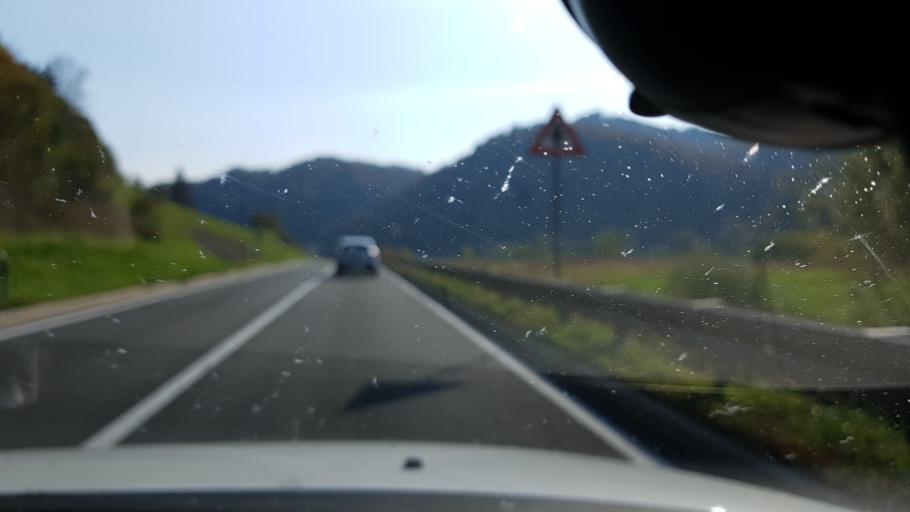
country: SI
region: Zetale
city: Zetale
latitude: 46.2186
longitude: 15.8439
